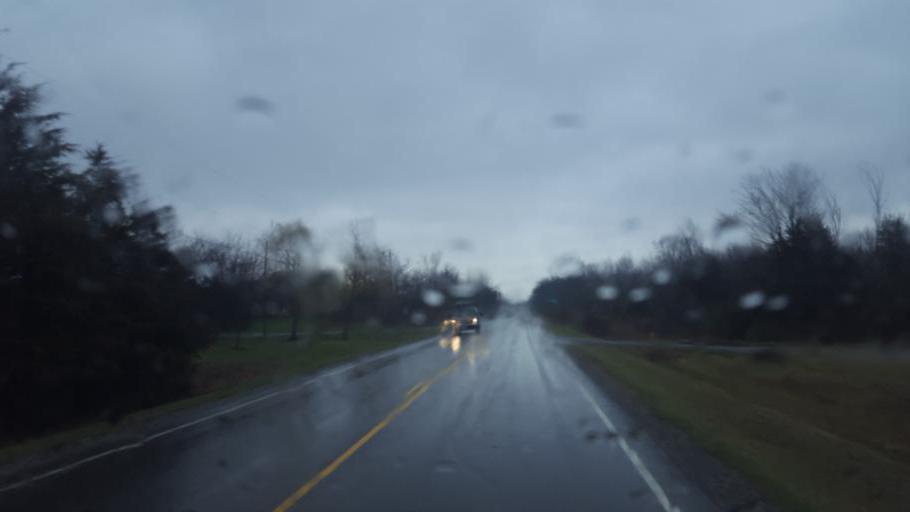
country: US
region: Ohio
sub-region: Delaware County
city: Lewis Center
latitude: 40.2673
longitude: -82.9847
